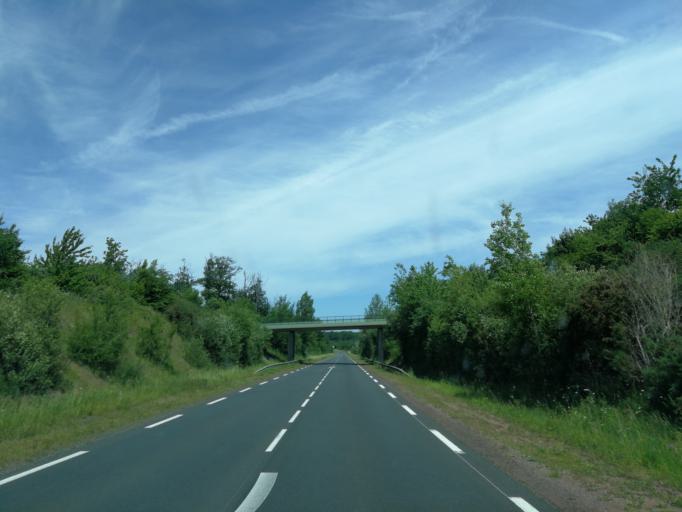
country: FR
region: Pays de la Loire
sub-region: Departement de la Vendee
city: Pissotte
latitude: 46.5090
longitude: -0.8152
